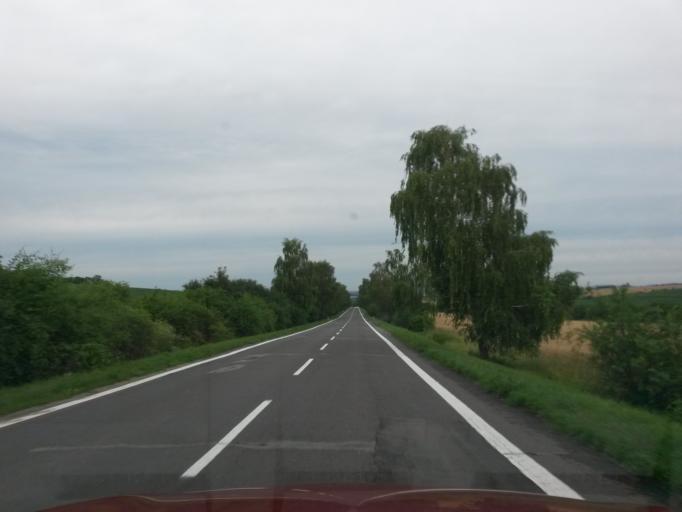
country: SK
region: Nitriansky
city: Zeliezovce
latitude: 48.1252
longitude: 18.7210
